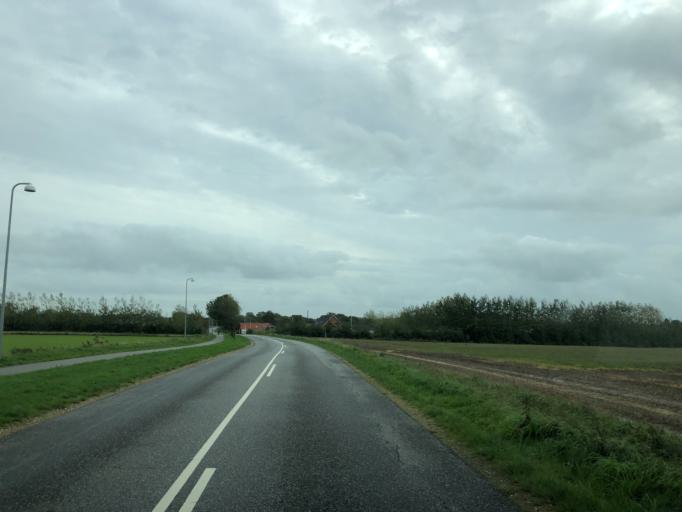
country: DK
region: Central Jutland
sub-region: Herning Kommune
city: Vildbjerg
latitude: 56.1844
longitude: 8.7456
